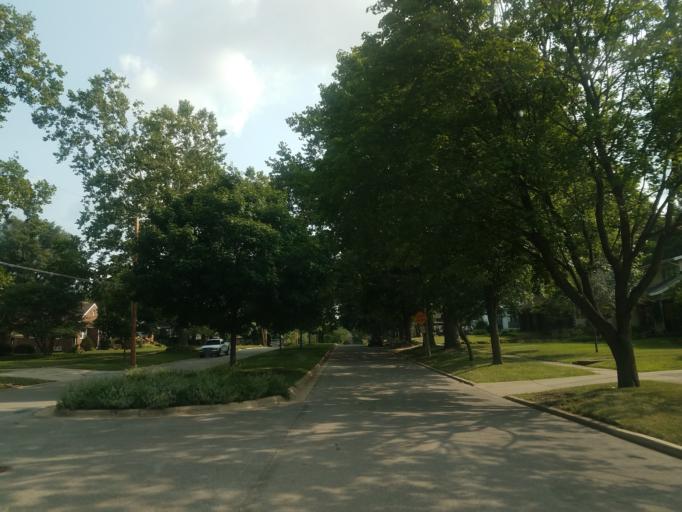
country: US
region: Illinois
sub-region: McLean County
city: Normal
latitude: 40.4997
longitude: -88.9856
